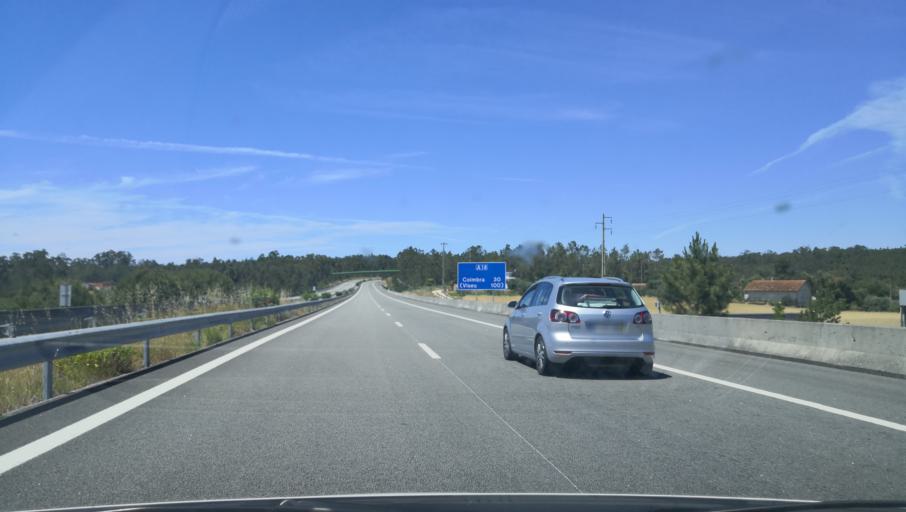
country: PT
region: Coimbra
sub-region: Montemor-O-Velho
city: Montemor-o-Velho
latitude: 40.2117
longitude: -8.6746
